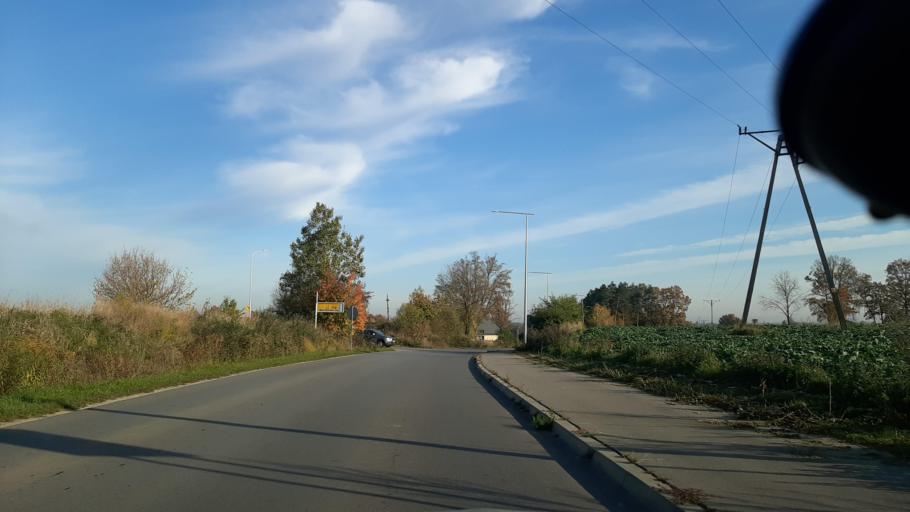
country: PL
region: Lublin Voivodeship
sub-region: Powiat lubelski
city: Lublin
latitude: 51.3060
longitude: 22.5614
